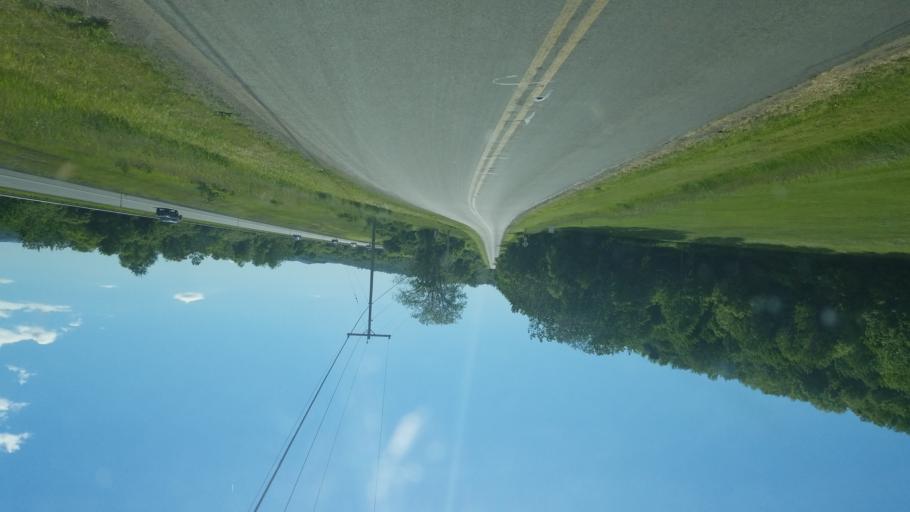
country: US
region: New York
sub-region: Montgomery County
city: Saint Johnsville
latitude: 42.9899
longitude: -74.6994
